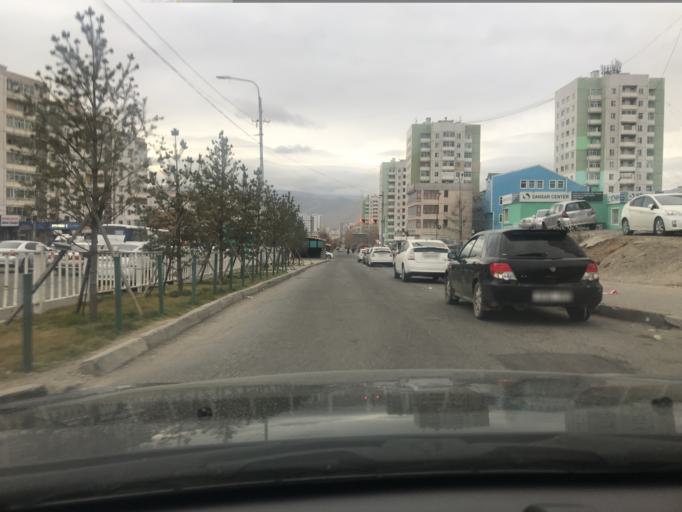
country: MN
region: Ulaanbaatar
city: Ulaanbaatar
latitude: 47.9251
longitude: 106.9414
